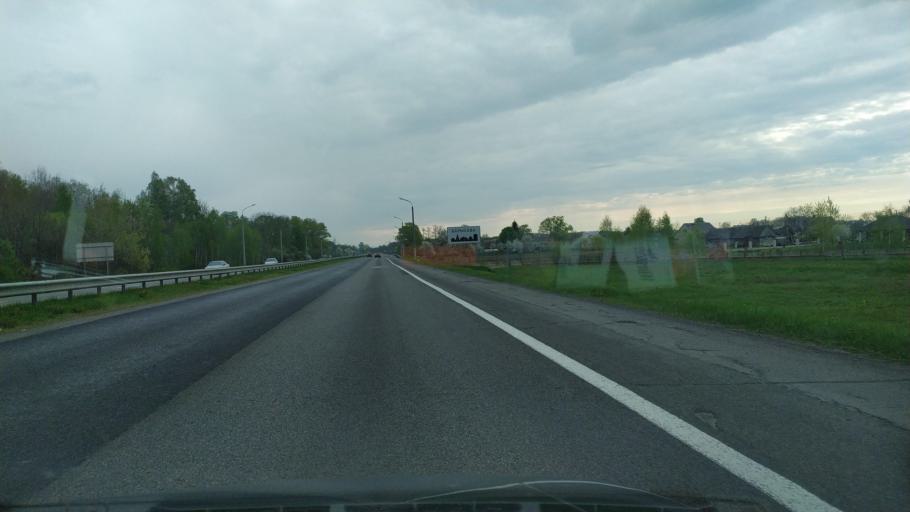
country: BY
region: Brest
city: Horad Kobryn
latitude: 52.1837
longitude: 24.3796
